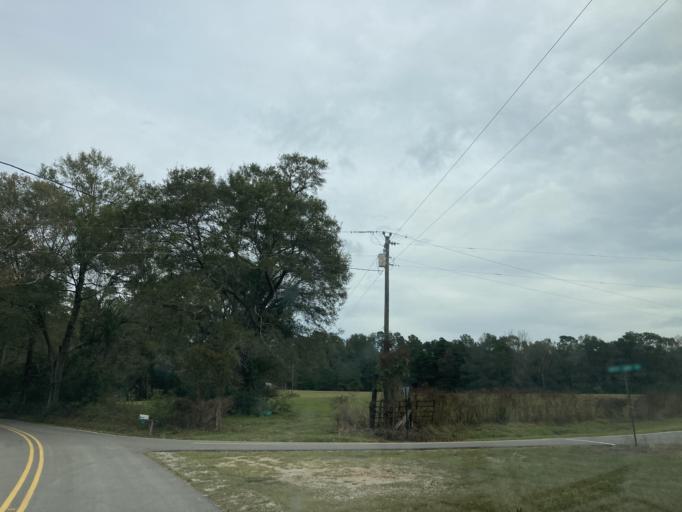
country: US
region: Mississippi
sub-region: Lamar County
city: Purvis
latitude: 31.1486
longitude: -89.4647
